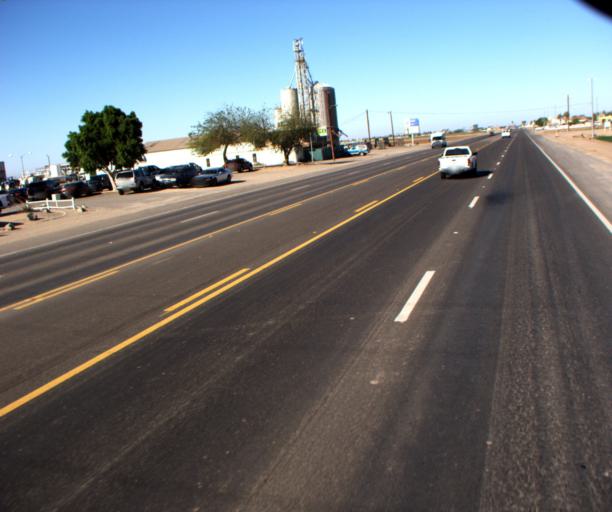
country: US
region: Arizona
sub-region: Yuma County
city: Somerton
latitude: 32.5968
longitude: -114.6865
